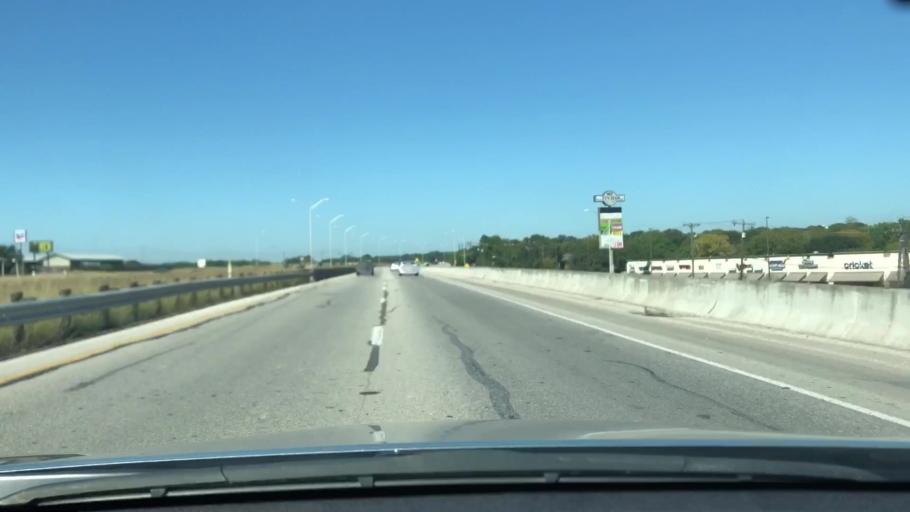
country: US
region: Texas
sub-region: Bexar County
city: Universal City
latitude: 29.5462
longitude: -98.3145
